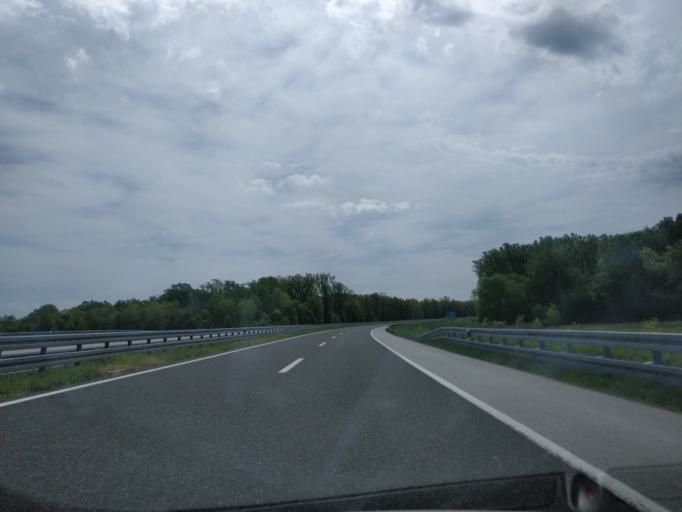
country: HR
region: Zagrebacka
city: Mraclin
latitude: 45.6445
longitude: 16.0926
